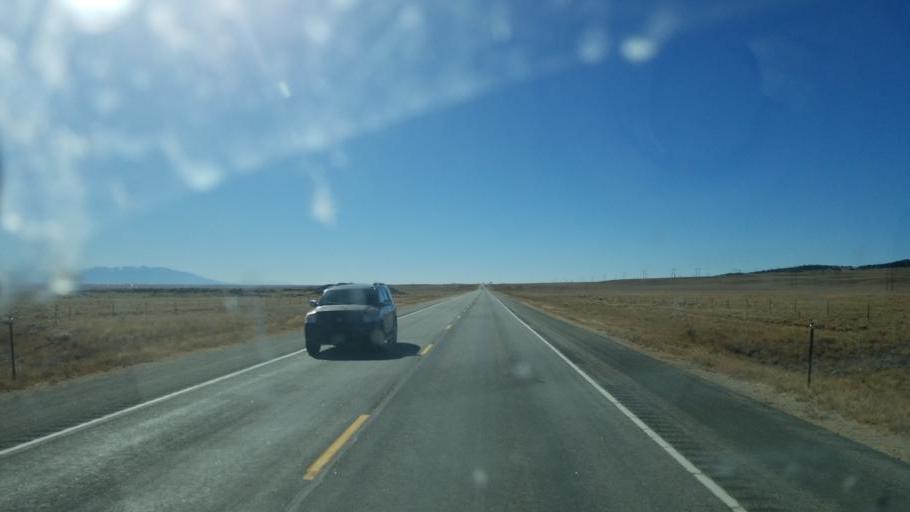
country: US
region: Colorado
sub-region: Saguache County
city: Saguache
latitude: 38.2082
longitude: -105.9425
